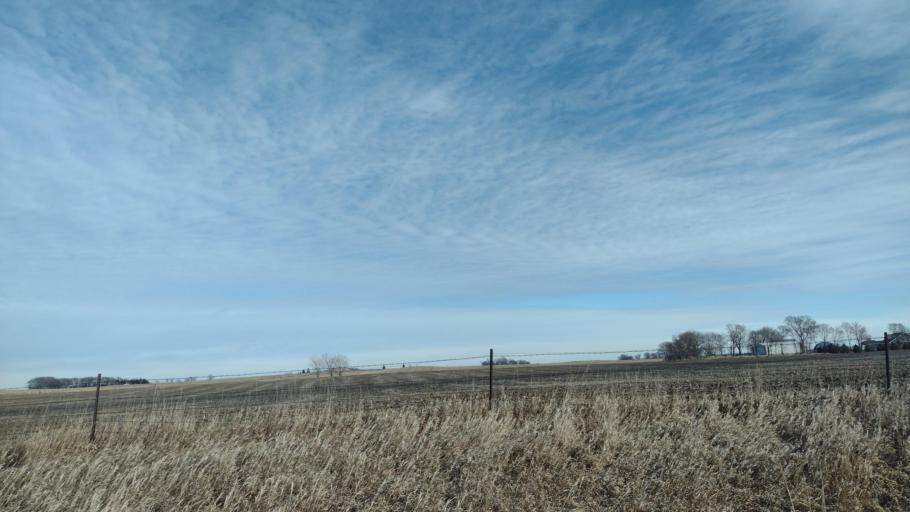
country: US
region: South Dakota
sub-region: Union County
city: Beresford
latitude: 42.9523
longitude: -96.8055
